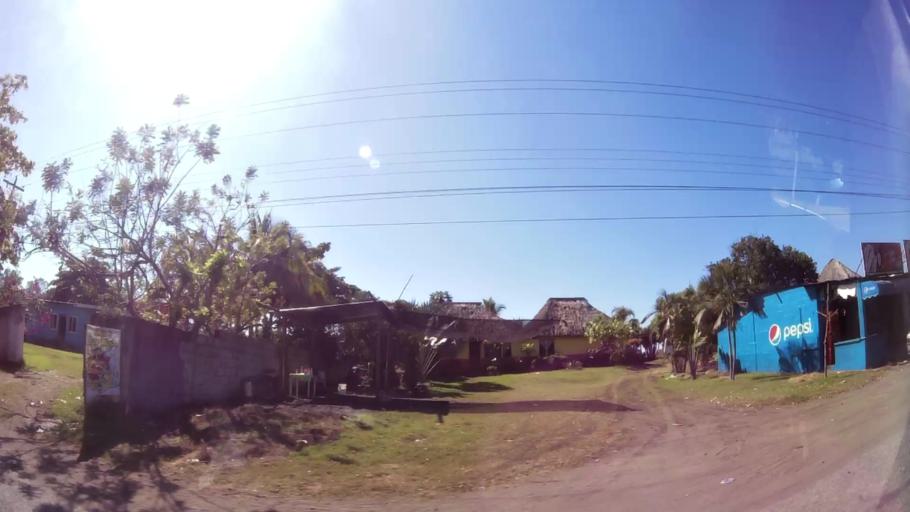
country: GT
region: Santa Rosa
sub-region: Municipio de Taxisco
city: Taxisco
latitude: 13.9130
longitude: -90.5384
